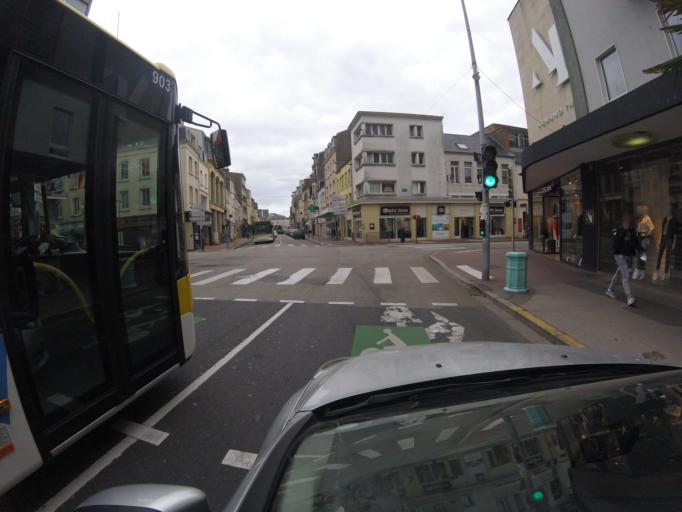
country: FR
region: Lower Normandy
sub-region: Departement de la Manche
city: Cherbourg-Octeville
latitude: 49.6379
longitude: -1.6252
